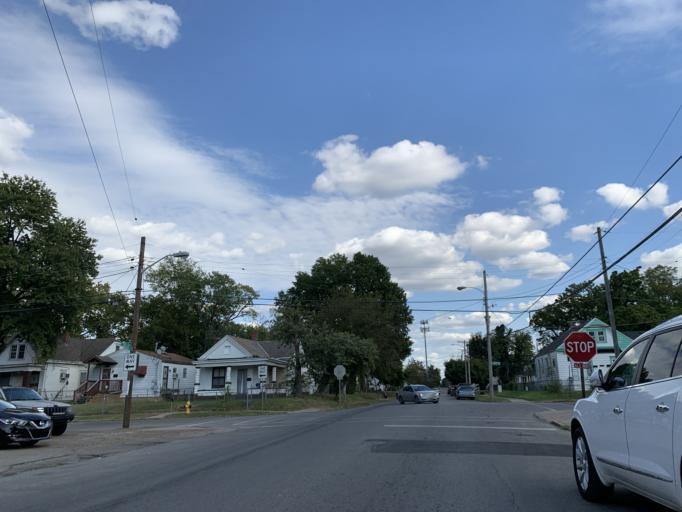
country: US
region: Indiana
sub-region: Floyd County
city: New Albany
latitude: 38.2456
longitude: -85.8063
